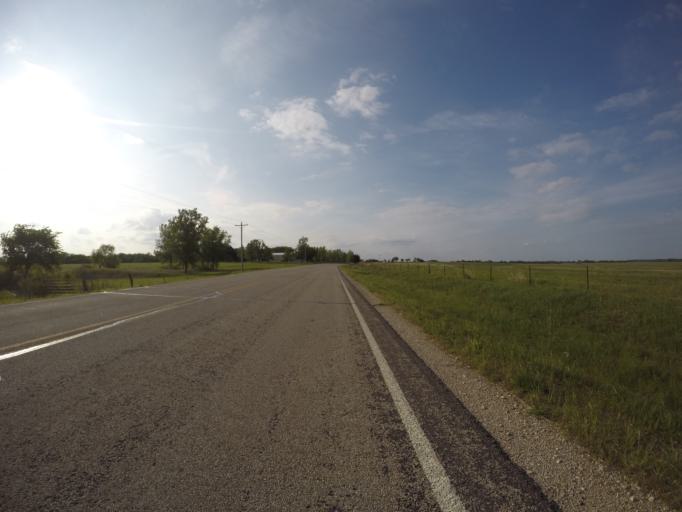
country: US
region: Kansas
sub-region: Pottawatomie County
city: Westmoreland
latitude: 39.4055
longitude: -96.6064
